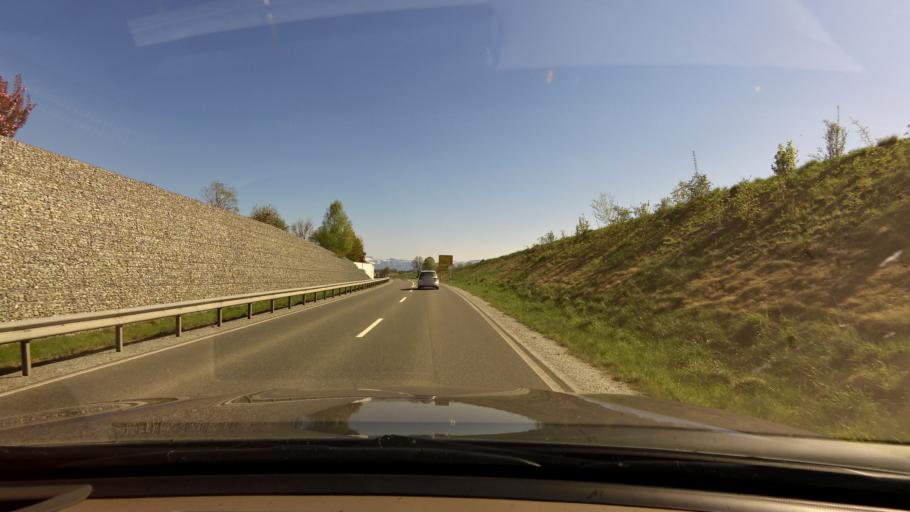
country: DE
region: Bavaria
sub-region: Upper Bavaria
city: Vogtareuth
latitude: 47.9431
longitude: 12.1781
